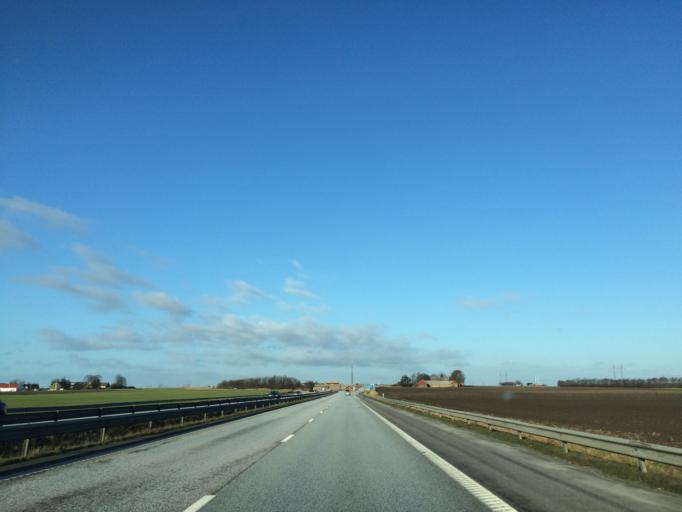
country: SE
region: Skane
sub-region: Lomma Kommun
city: Lomma
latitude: 55.7168
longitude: 13.0927
